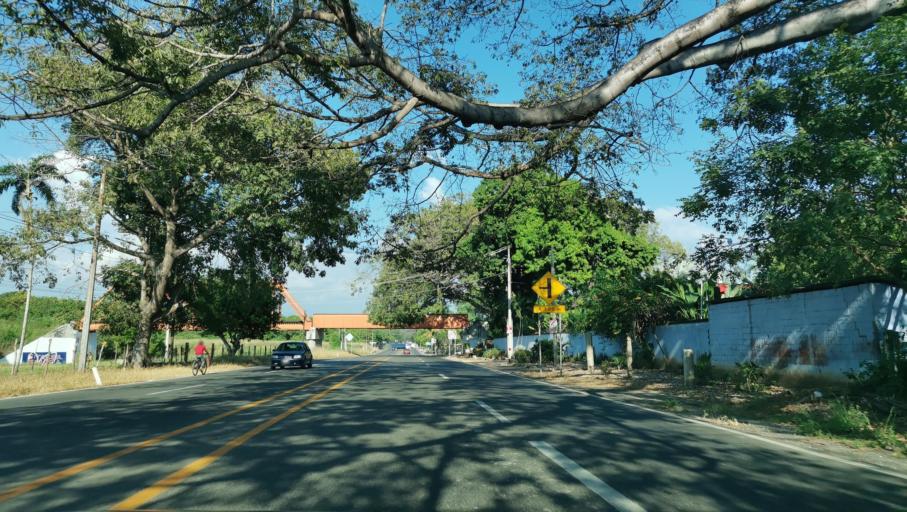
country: MX
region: Chiapas
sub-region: Tapachula
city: Congregacion Reforma
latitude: 14.8177
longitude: -92.3424
